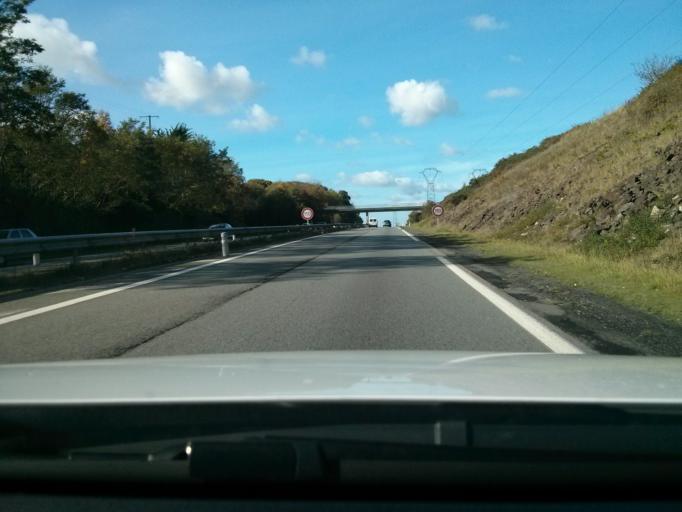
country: FR
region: Brittany
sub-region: Departement des Cotes-d'Armor
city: Pleudihen-sur-Rance
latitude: 48.5366
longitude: -1.9790
